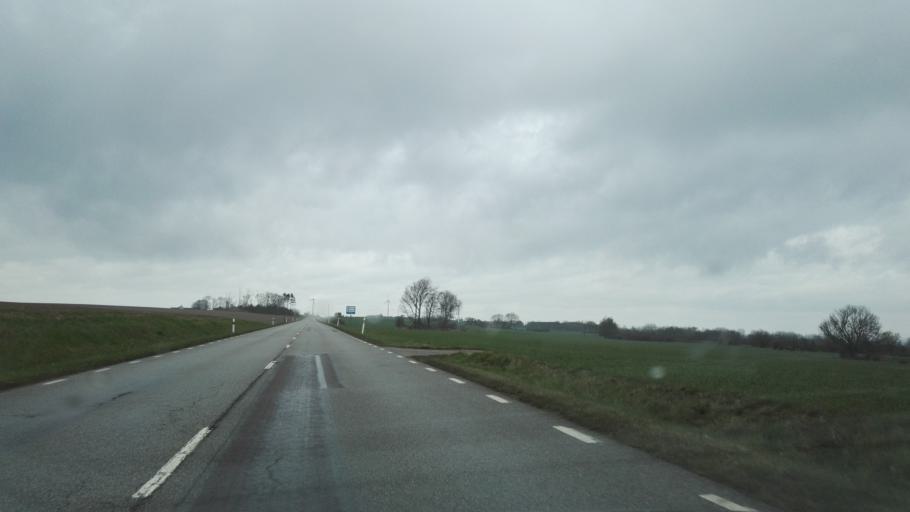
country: SE
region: Skane
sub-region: Simrishamns Kommun
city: Simrishamn
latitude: 55.5239
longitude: 14.3395
